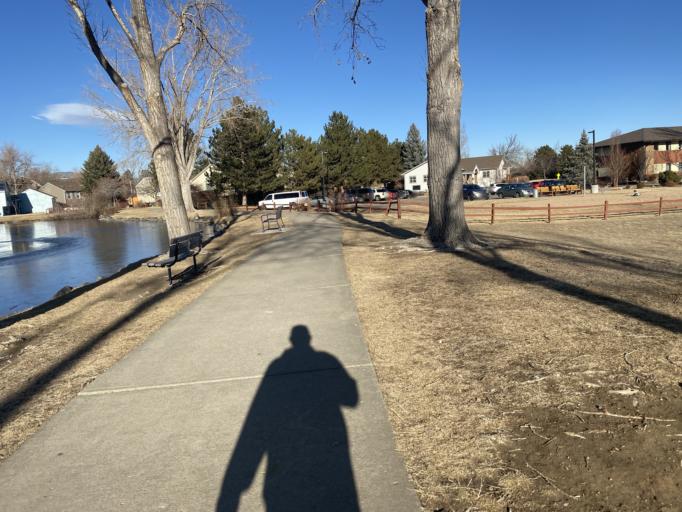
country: US
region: Colorado
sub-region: Jefferson County
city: Arvada
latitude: 39.8098
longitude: -105.1420
